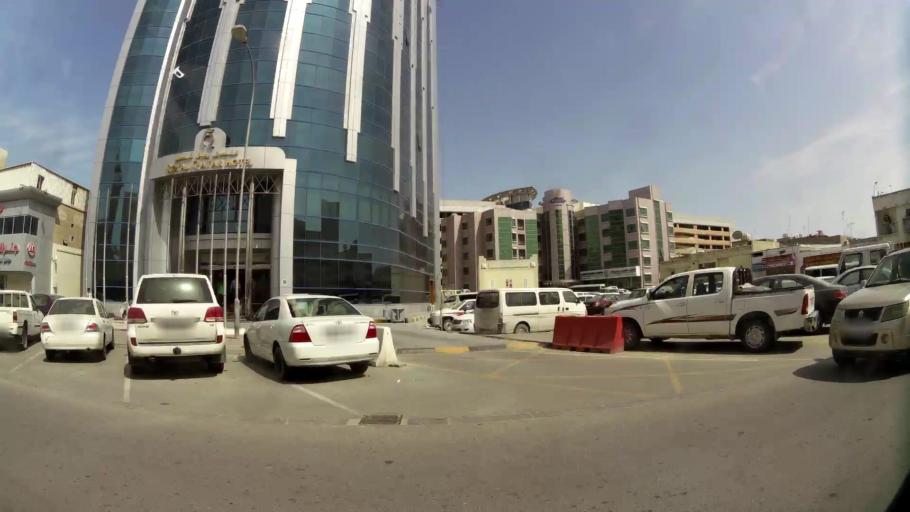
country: QA
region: Baladiyat ad Dawhah
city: Doha
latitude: 25.2827
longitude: 51.5324
